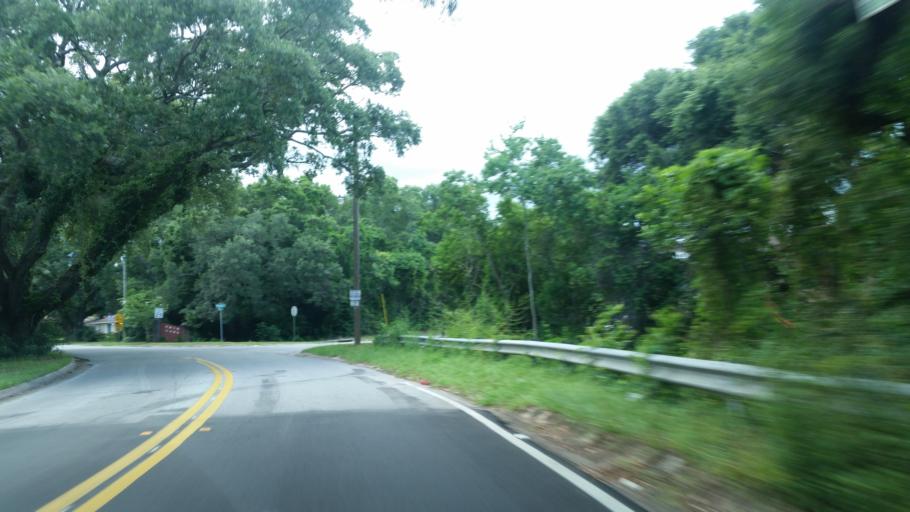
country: US
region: Florida
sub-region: Escambia County
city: West Pensacola
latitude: 30.4102
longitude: -87.2818
